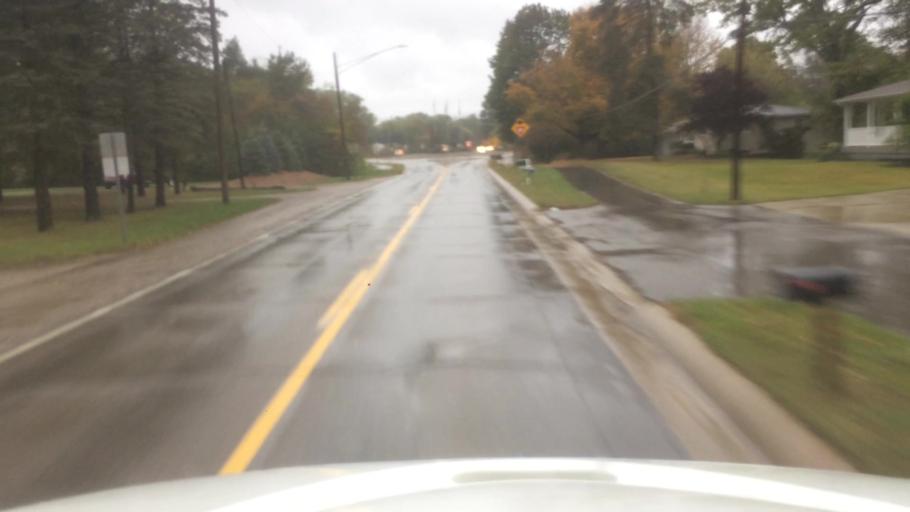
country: US
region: Michigan
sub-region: Oakland County
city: Oxford
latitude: 42.7841
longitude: -83.3176
